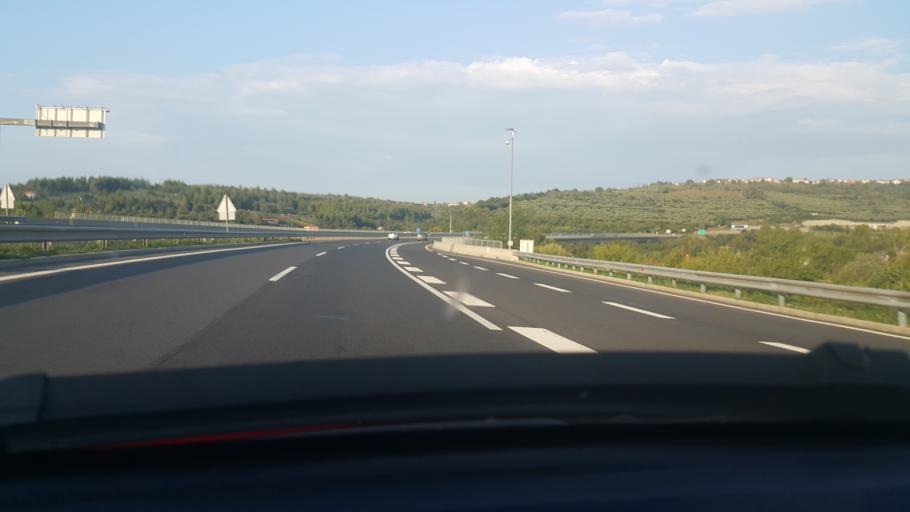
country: SI
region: Koper-Capodistria
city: Prade
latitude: 45.5572
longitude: 13.7810
